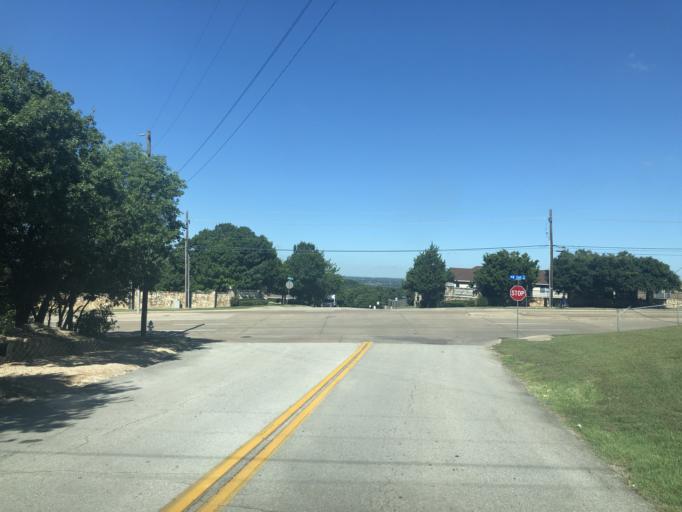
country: US
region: Texas
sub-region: Dallas County
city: Duncanville
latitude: 32.6562
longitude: -96.9425
